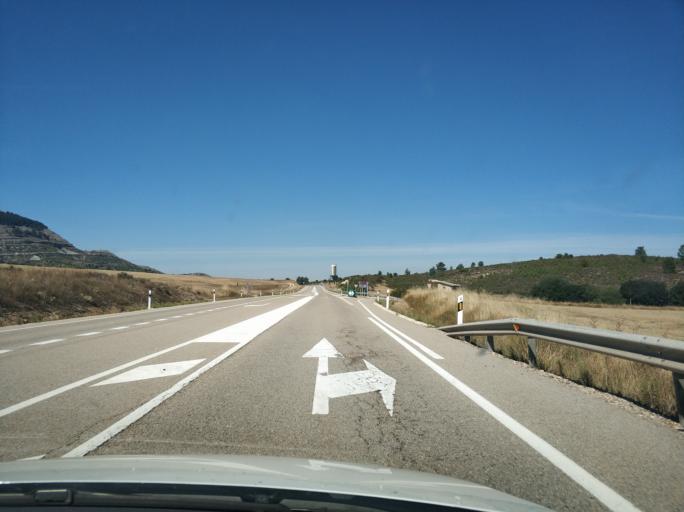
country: ES
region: Castille and Leon
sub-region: Provincia de Burgos
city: Mambrillas de Lara
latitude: 42.0984
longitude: -3.4927
